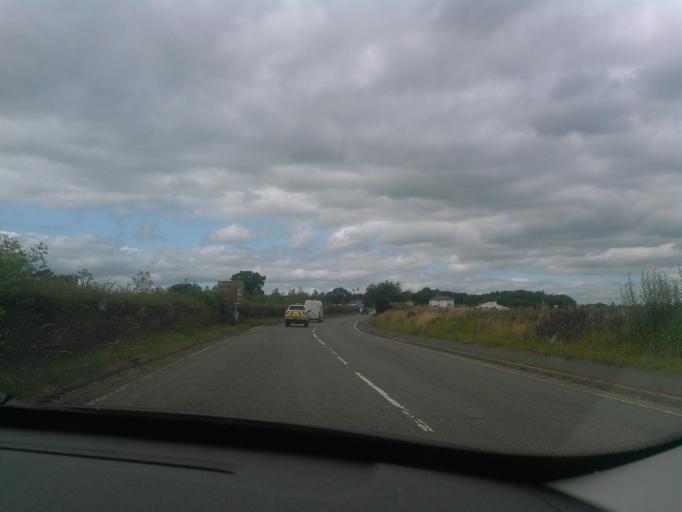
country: GB
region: England
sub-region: Shropshire
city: Berrington
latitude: 52.6892
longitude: -2.7043
